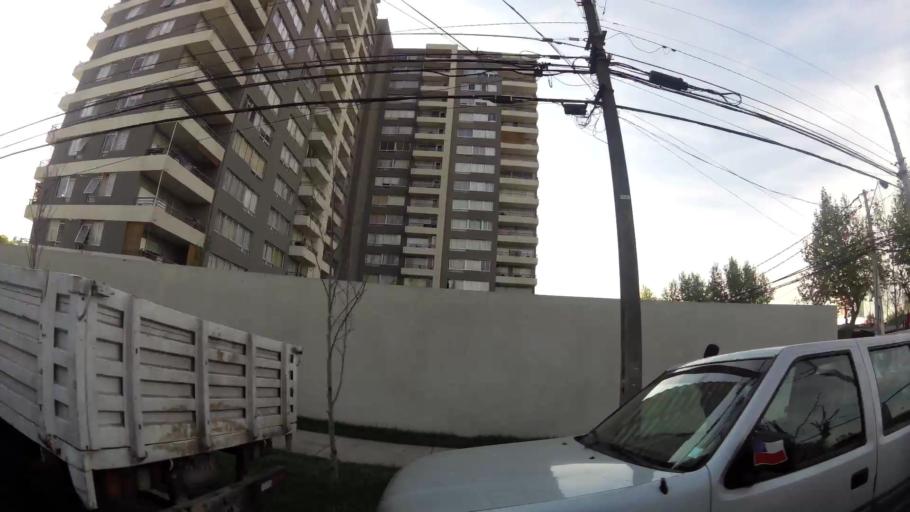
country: CL
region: Santiago Metropolitan
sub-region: Provincia de Santiago
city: Santiago
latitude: -33.5088
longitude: -70.6658
